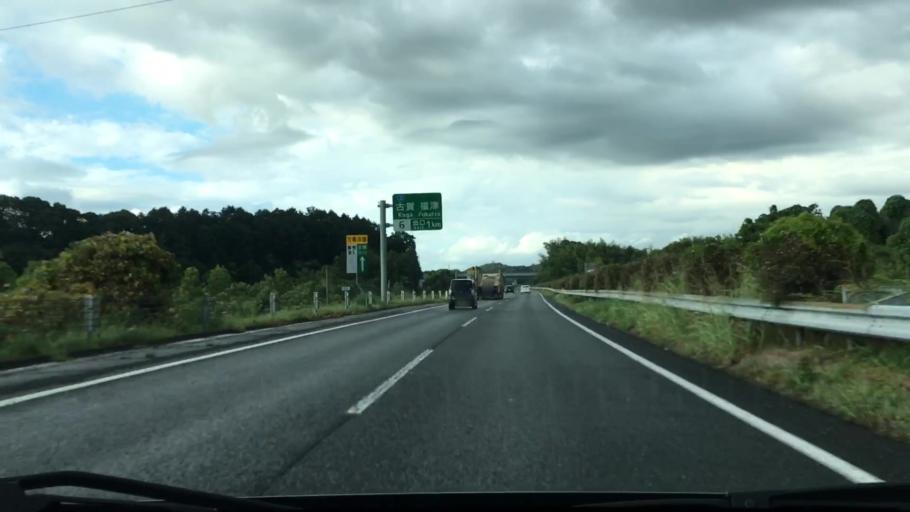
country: JP
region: Fukuoka
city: Koga
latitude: 33.7081
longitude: 130.4870
